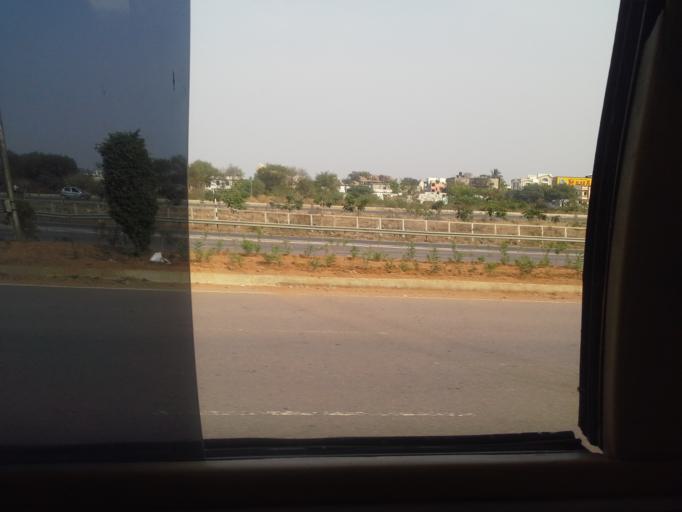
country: IN
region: Telangana
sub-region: Hyderabad
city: Hyderabad
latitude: 17.3905
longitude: 78.3517
